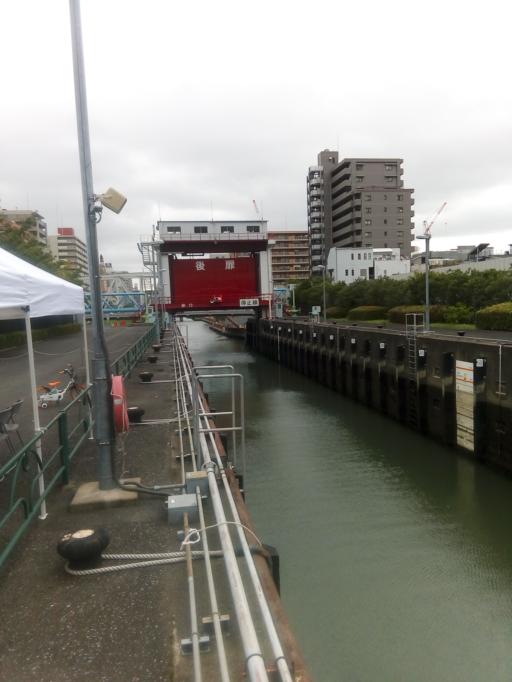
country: JP
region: Tokyo
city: Urayasu
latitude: 35.6844
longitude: 139.8122
